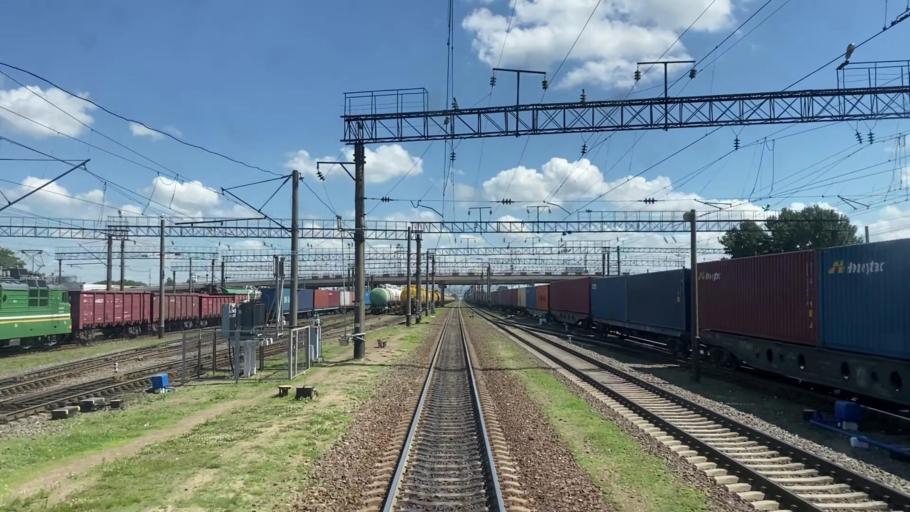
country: BY
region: Brest
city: Baranovichi
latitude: 53.1381
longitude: 26.0079
